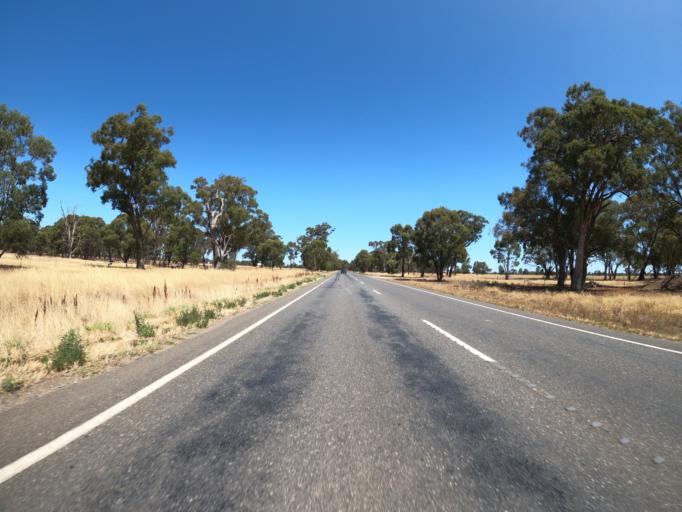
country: AU
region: New South Wales
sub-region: Corowa Shire
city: Corowa
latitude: -36.0244
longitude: 146.4151
